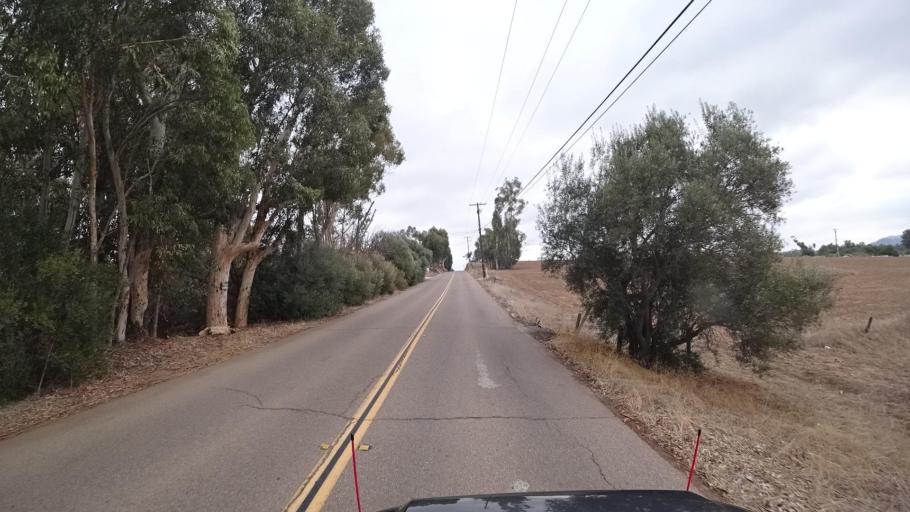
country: US
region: California
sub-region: San Diego County
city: Ramona
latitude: 33.0368
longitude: -116.8623
